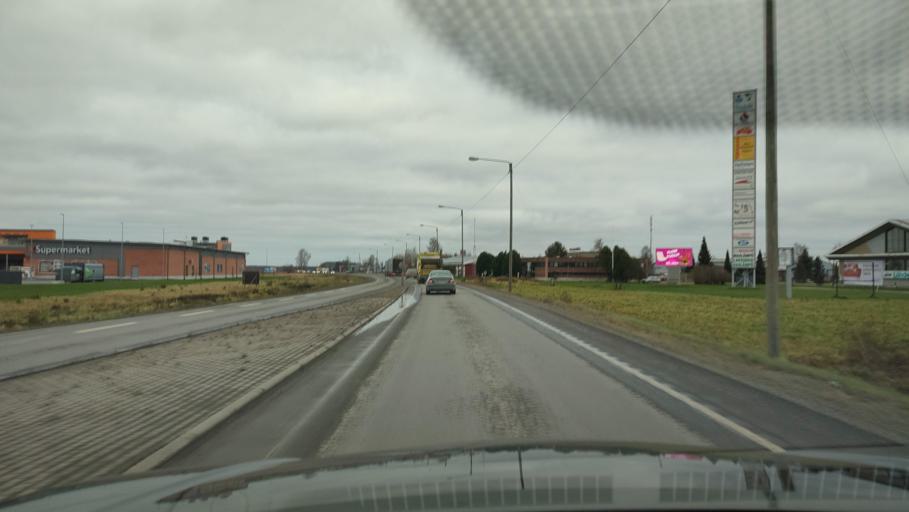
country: FI
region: Southern Ostrobothnia
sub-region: Seinaejoki
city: Ilmajoki
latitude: 62.7301
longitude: 22.5981
